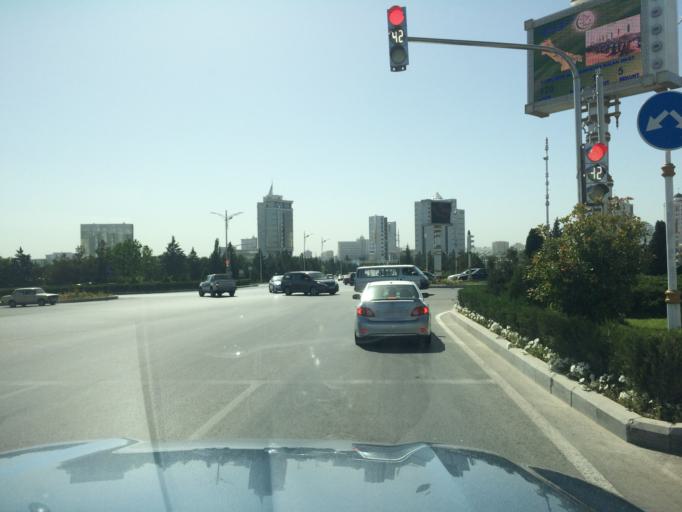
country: TM
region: Ahal
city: Ashgabat
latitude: 37.9273
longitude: 58.3716
